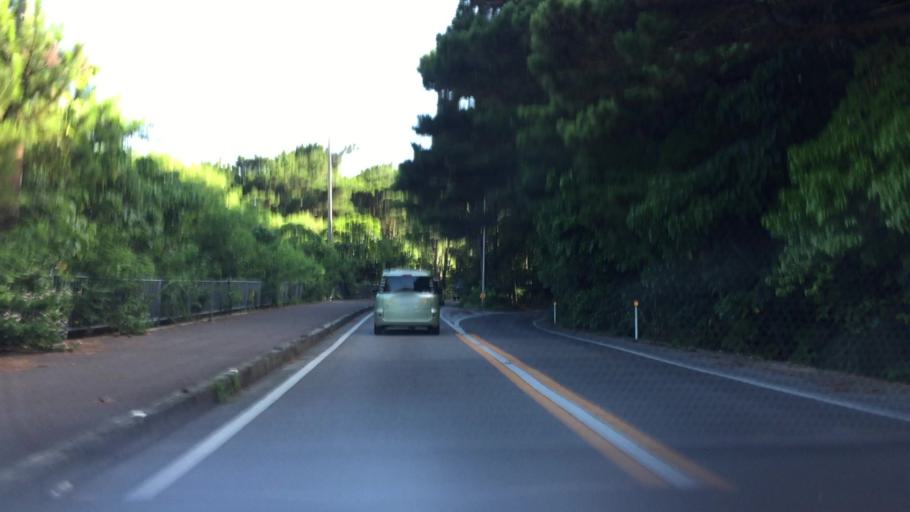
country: JP
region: Okinawa
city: Ishigaki
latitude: 24.4483
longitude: 124.1289
